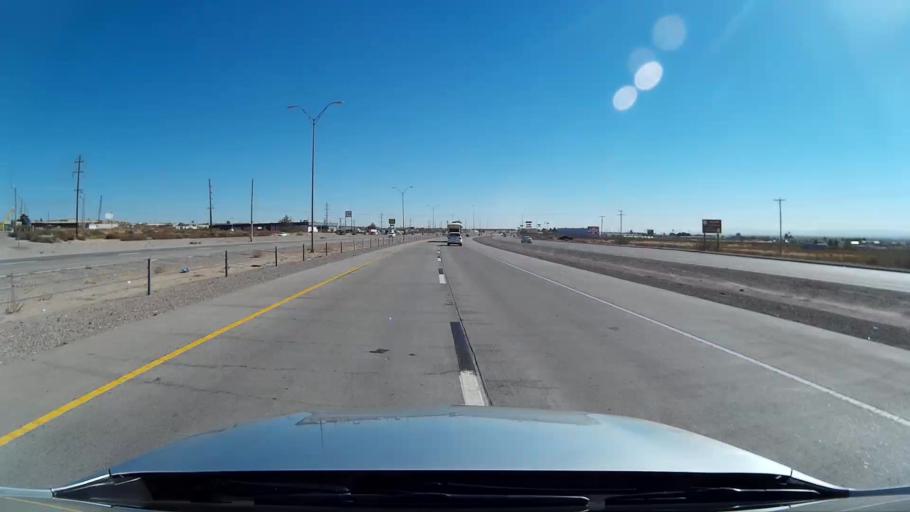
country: US
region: Texas
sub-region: El Paso County
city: Sparks
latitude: 31.6677
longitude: -106.2465
